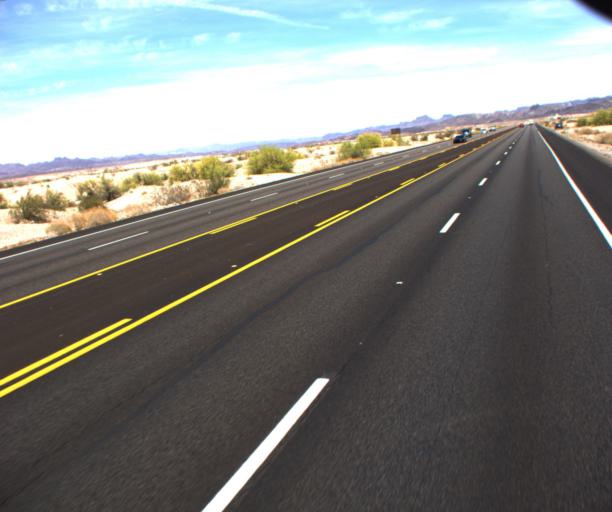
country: US
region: Arizona
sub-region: La Paz County
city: Parker
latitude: 34.1609
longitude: -114.2638
